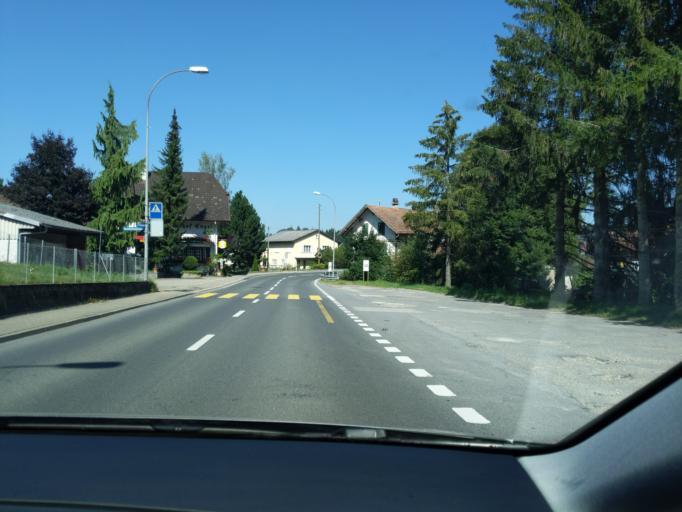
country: CH
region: Lucerne
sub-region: Willisau District
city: Zell
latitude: 47.1277
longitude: 7.9034
